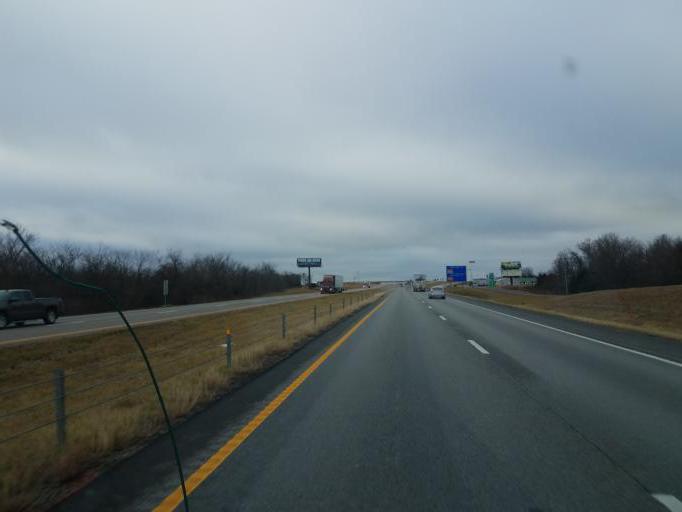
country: US
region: Missouri
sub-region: Webster County
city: Marshfield
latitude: 37.5115
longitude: -92.8383
